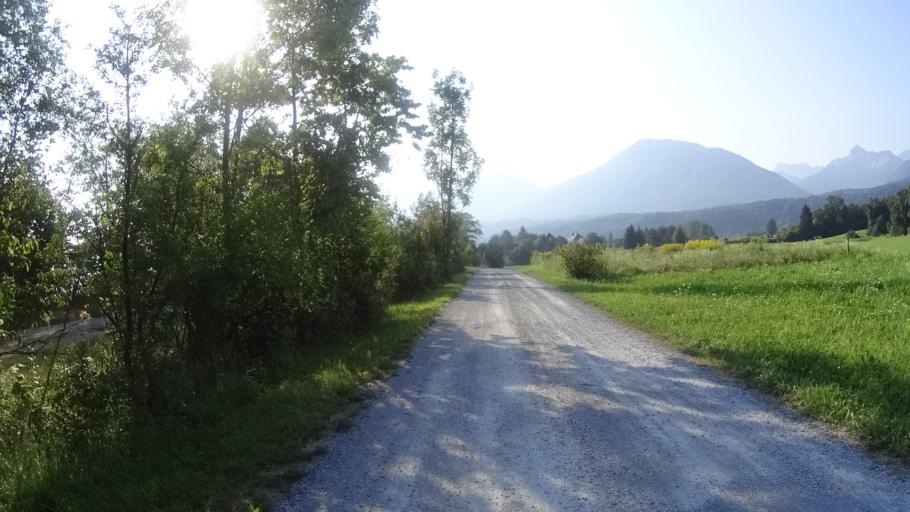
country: AT
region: Carinthia
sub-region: Politischer Bezirk Klagenfurt Land
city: Ludmannsdorf
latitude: 46.5308
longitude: 14.1429
